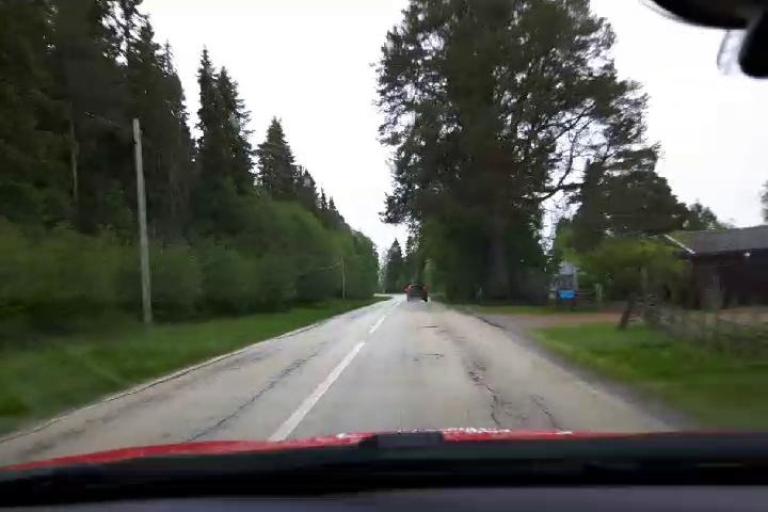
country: SE
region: Jaemtland
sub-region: Bergs Kommun
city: Hoverberg
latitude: 62.7864
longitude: 14.4366
